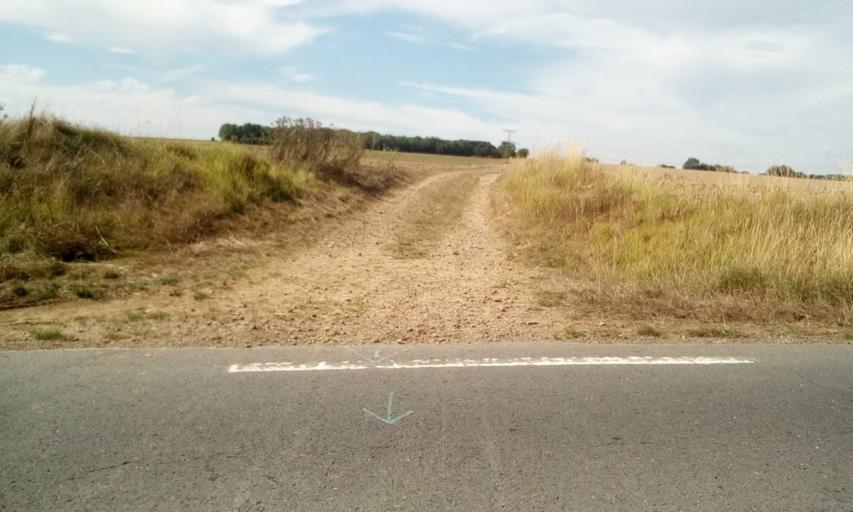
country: FR
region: Lower Normandy
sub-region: Departement du Calvados
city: Fontaine-Etoupefour
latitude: 49.1141
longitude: -0.4517
